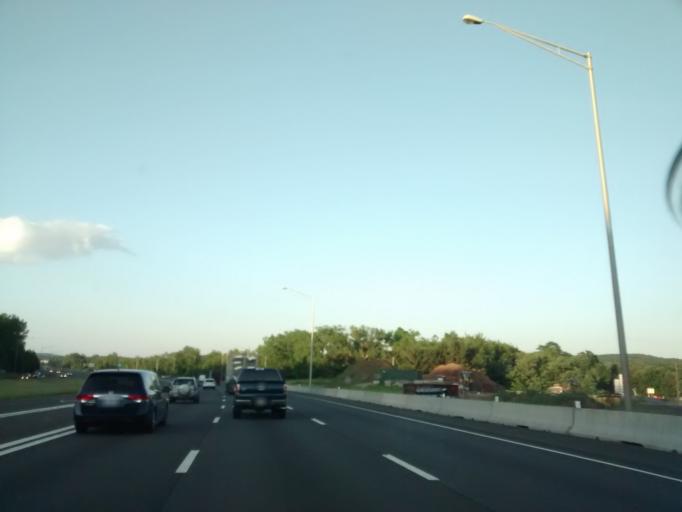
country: US
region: Connecticut
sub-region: Hartford County
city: Manchester
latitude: 41.8117
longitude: -72.5195
